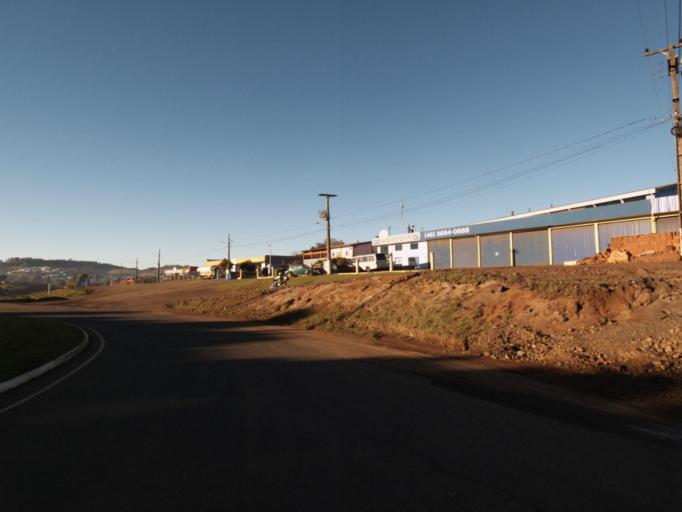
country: BR
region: Santa Catarina
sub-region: Sao Lourenco Do Oeste
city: Sao Lourenco dOeste
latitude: -26.7747
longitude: -53.2036
